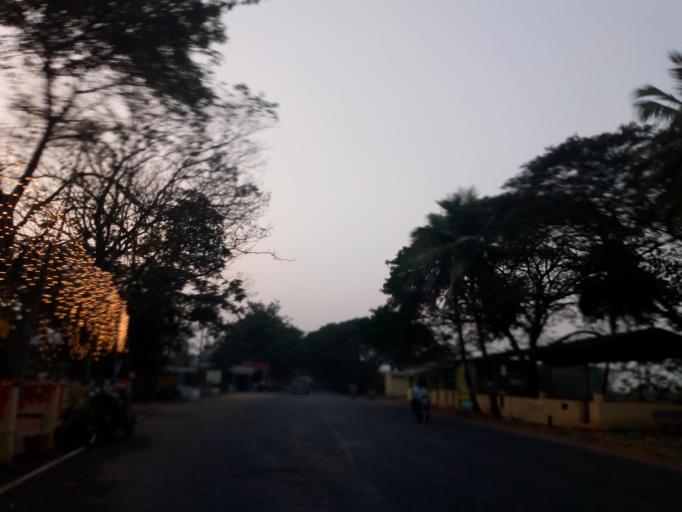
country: IN
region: Andhra Pradesh
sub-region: West Godavari
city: Tadepallegudem
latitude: 16.8173
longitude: 81.4929
